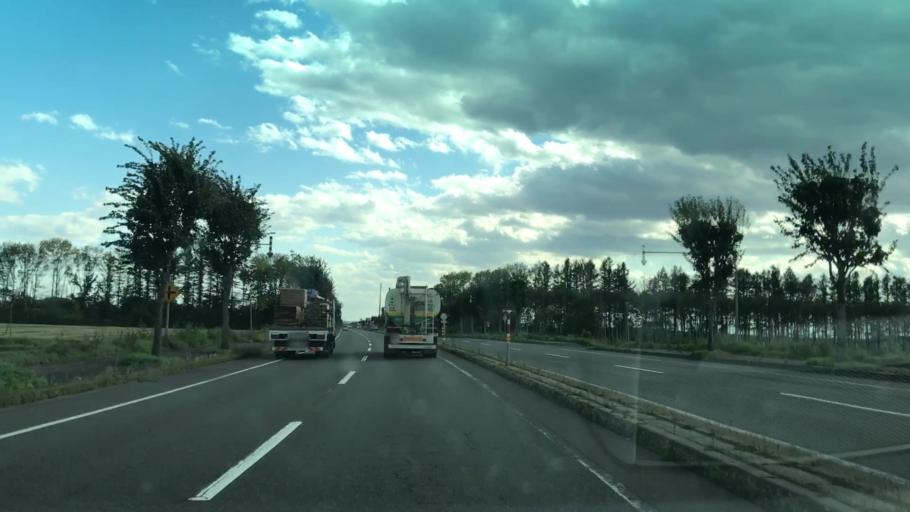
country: JP
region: Hokkaido
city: Otofuke
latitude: 43.0063
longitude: 143.1808
